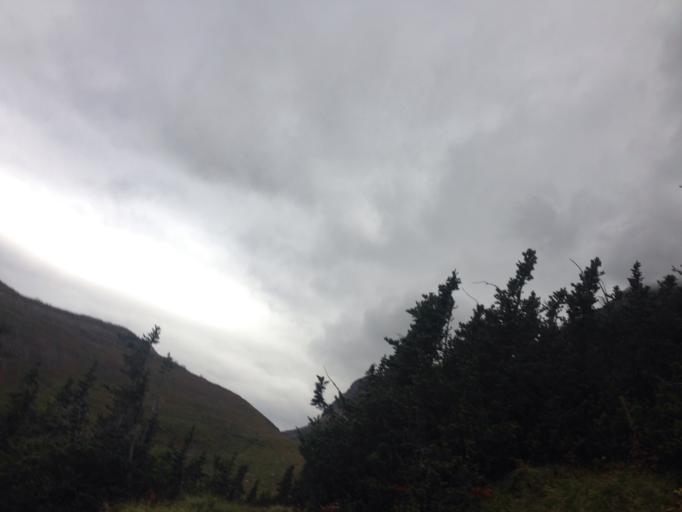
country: US
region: Montana
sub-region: Flathead County
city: Columbia Falls
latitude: 48.7297
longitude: -113.7192
